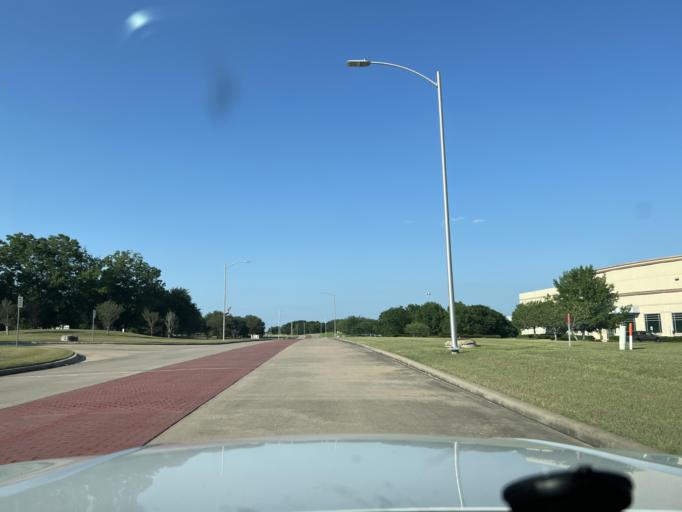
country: US
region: Texas
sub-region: Washington County
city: Brenham
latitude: 30.1384
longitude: -96.3680
